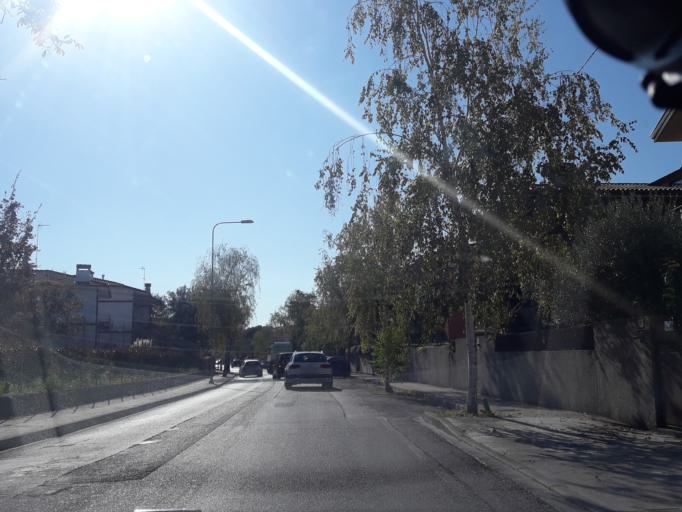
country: IT
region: Friuli Venezia Giulia
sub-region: Provincia di Udine
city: Udine
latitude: 46.0869
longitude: 13.2419
